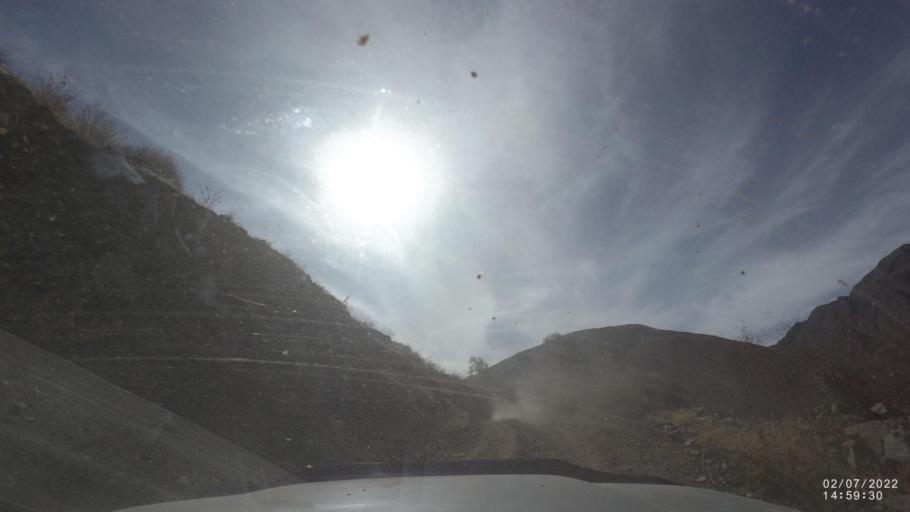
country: BO
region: Cochabamba
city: Irpa Irpa
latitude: -17.8535
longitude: -66.4399
